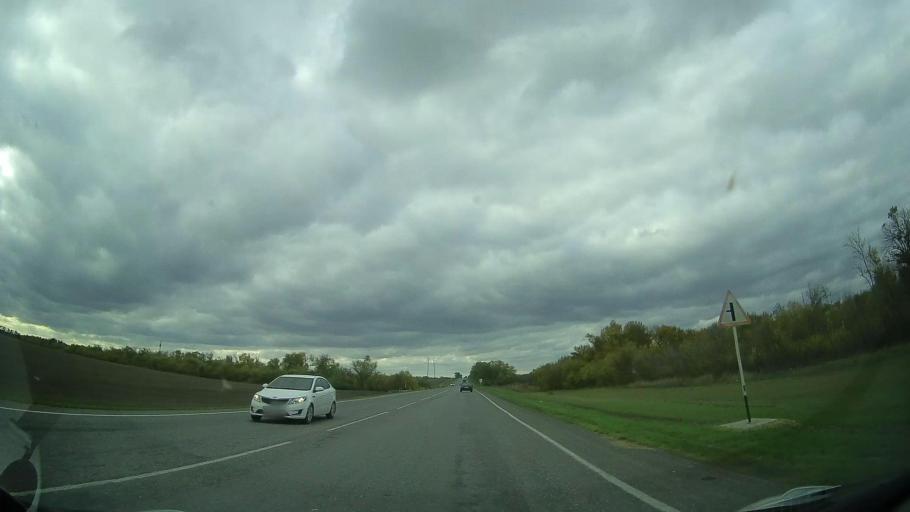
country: RU
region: Rostov
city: Zernograd
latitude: 46.8206
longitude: 40.2576
